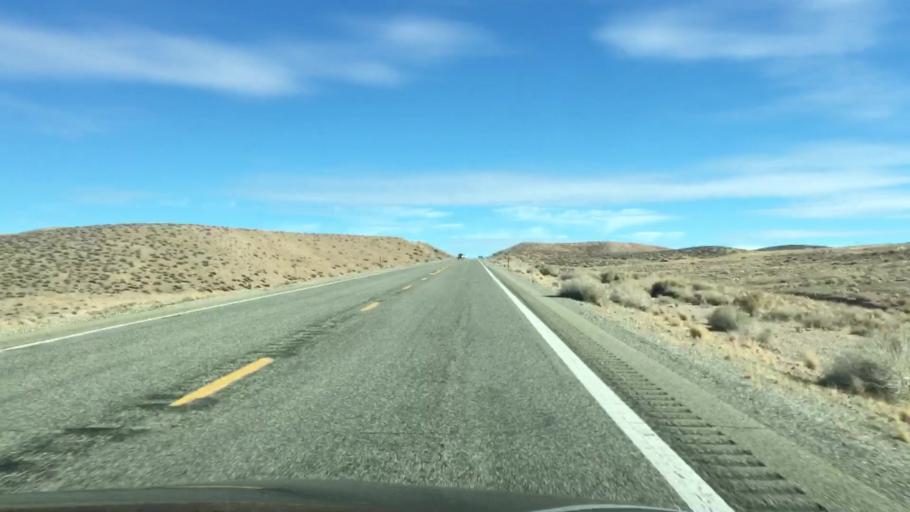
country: US
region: Nevada
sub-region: Lyon County
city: Yerington
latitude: 39.0455
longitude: -118.9637
